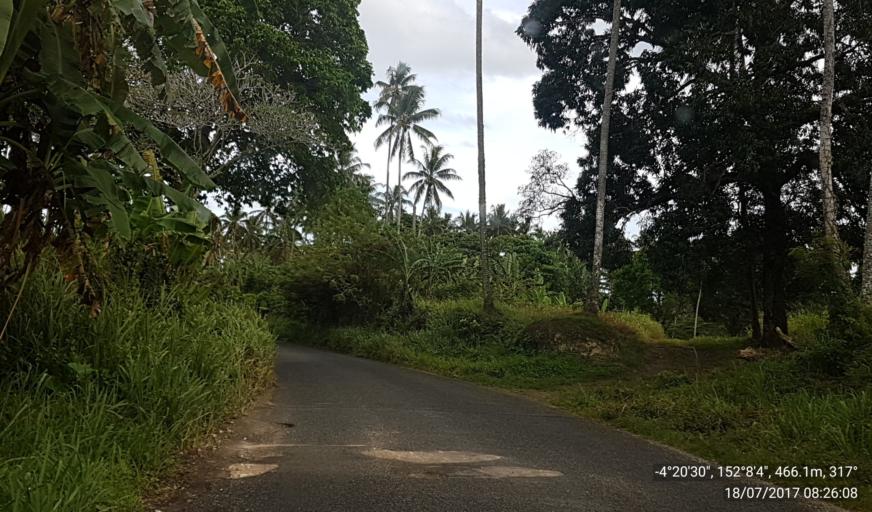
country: PG
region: East New Britain
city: Kokopo
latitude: -4.3419
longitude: 152.1347
